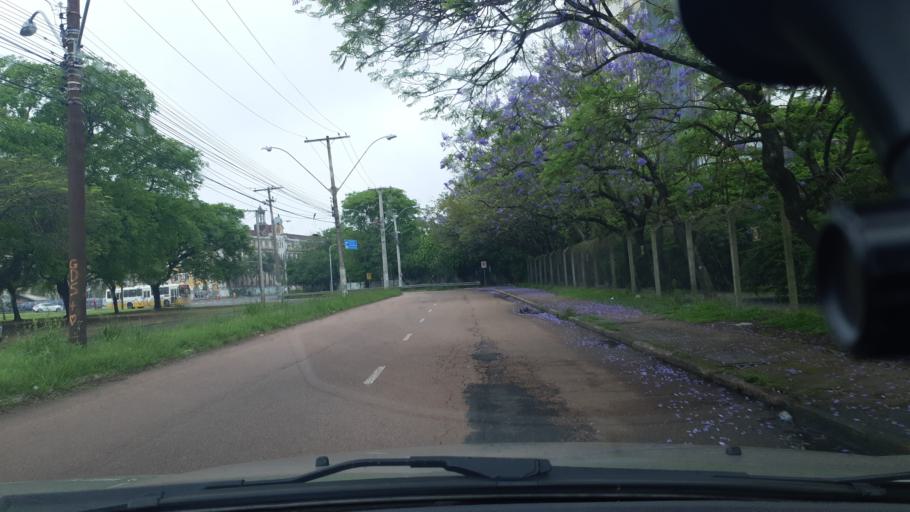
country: BR
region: Rio Grande do Sul
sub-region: Porto Alegre
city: Porto Alegre
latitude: -30.0395
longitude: -51.2300
